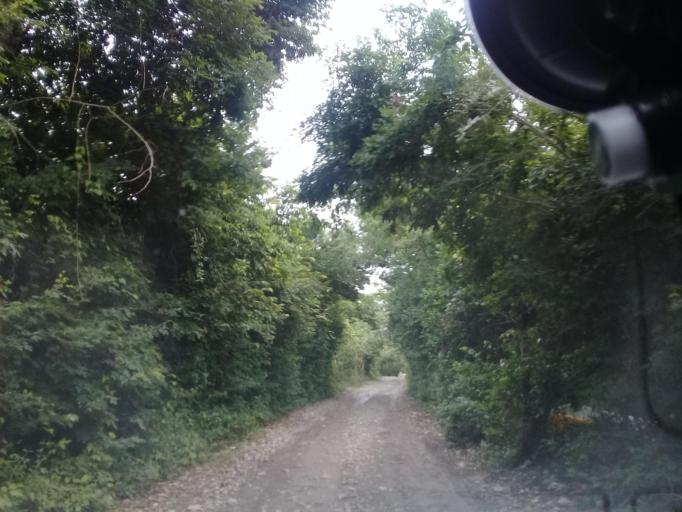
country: MX
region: Veracruz
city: Platon Sanchez
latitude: 21.2145
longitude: -98.3646
